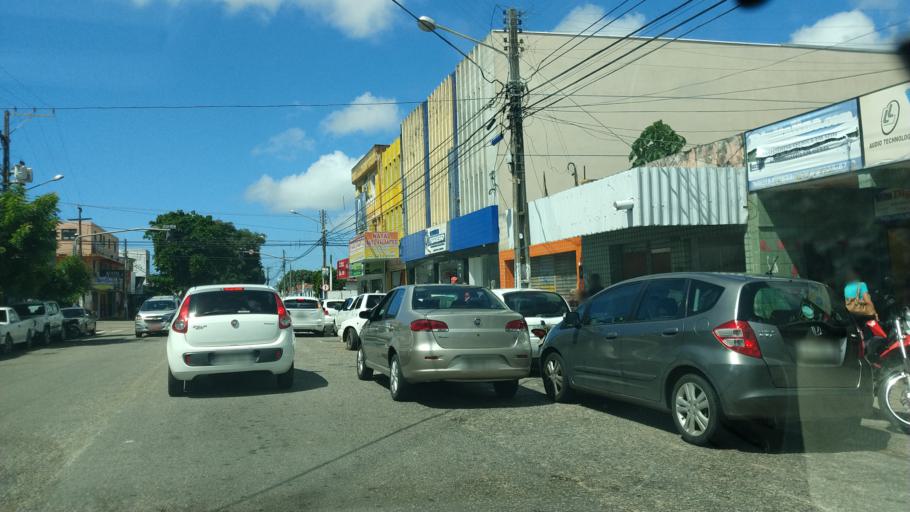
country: BR
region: Rio Grande do Norte
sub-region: Natal
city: Natal
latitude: -5.7978
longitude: -35.2197
